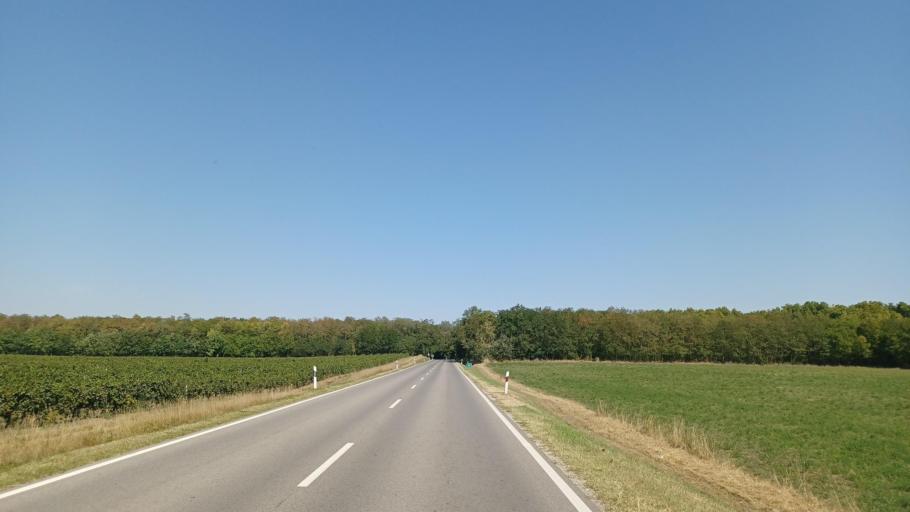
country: HU
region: Tolna
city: Nagydorog
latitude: 46.6909
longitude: 18.6729
